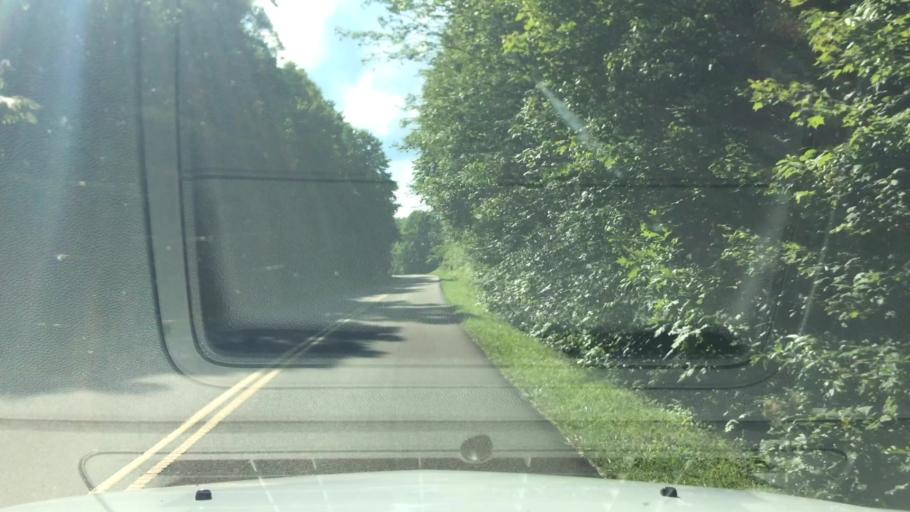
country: US
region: North Carolina
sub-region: Watauga County
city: Foscoe
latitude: 36.1315
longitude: -81.7533
